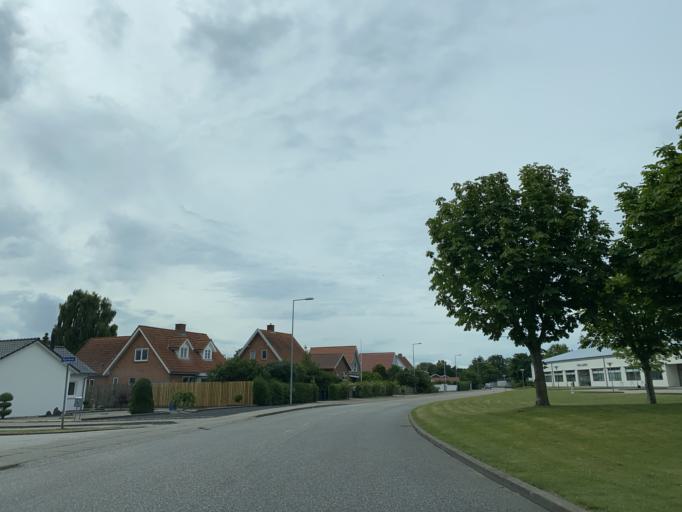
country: DK
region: South Denmark
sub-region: Sonderborg Kommune
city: Sonderborg
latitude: 54.9215
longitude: 9.8244
